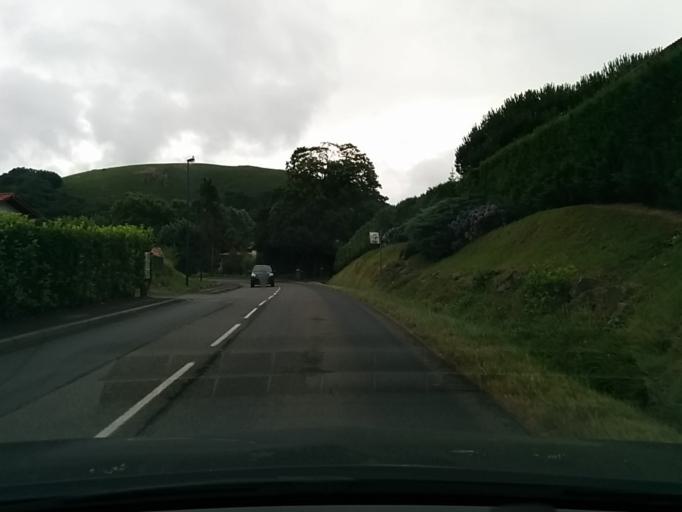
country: FR
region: Aquitaine
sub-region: Departement des Pyrenees-Atlantiques
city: Saint-Pee-sur-Nivelle
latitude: 43.3326
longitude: -1.5475
